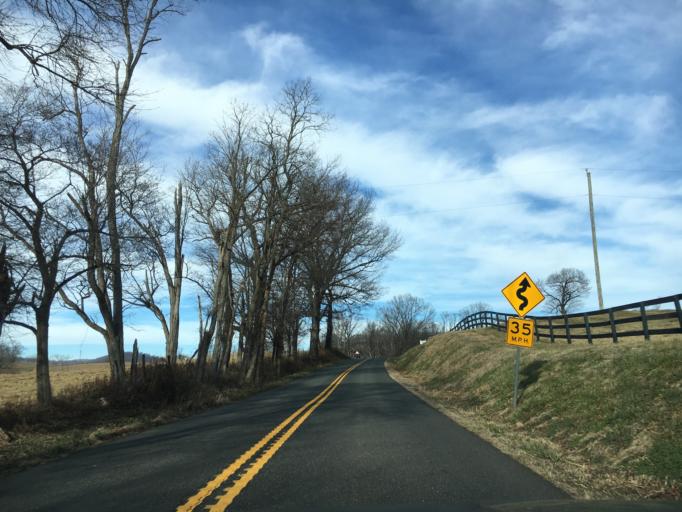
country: US
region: Virginia
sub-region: Warren County
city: Apple Mountain Lake
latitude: 38.8612
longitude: -77.9948
